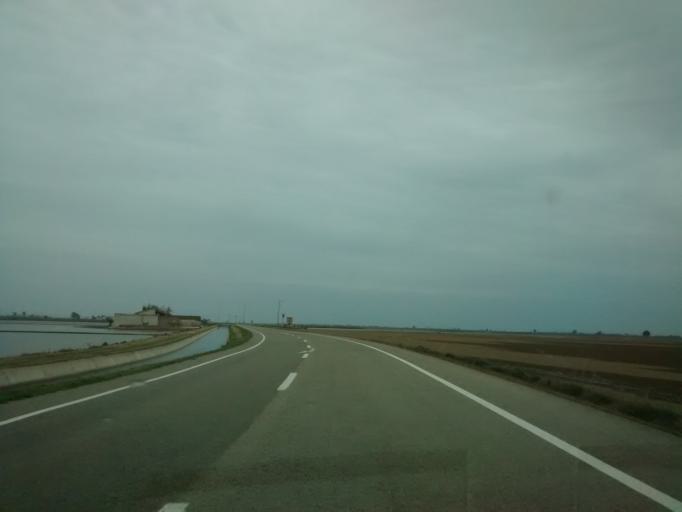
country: ES
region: Catalonia
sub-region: Provincia de Tarragona
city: Deltebre
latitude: 40.6980
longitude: 0.6785
